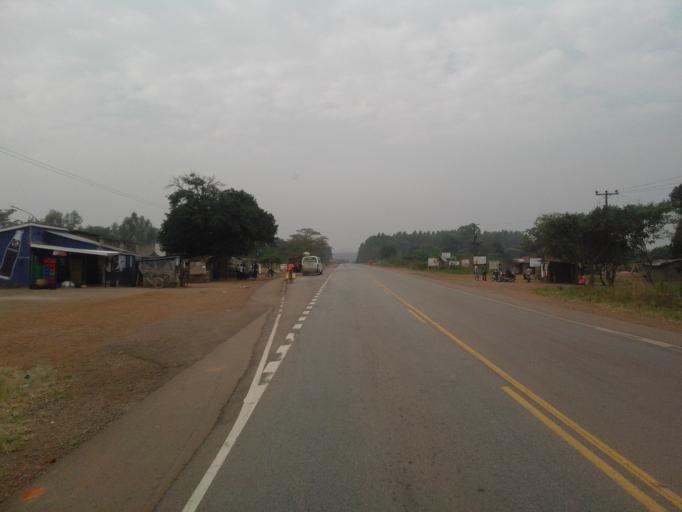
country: UG
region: Eastern Region
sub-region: Busia District
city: Busia
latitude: 0.6000
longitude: 34.0639
